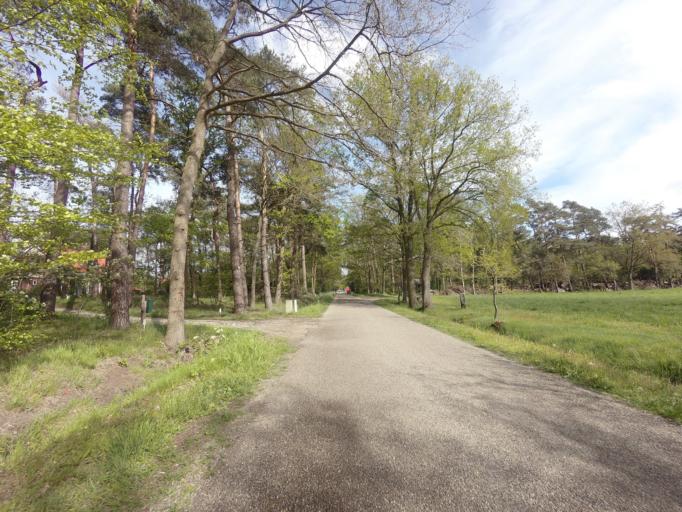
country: NL
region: Overijssel
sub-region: Gemeente Hengelo
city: Hengelo
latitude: 52.1955
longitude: 6.8100
